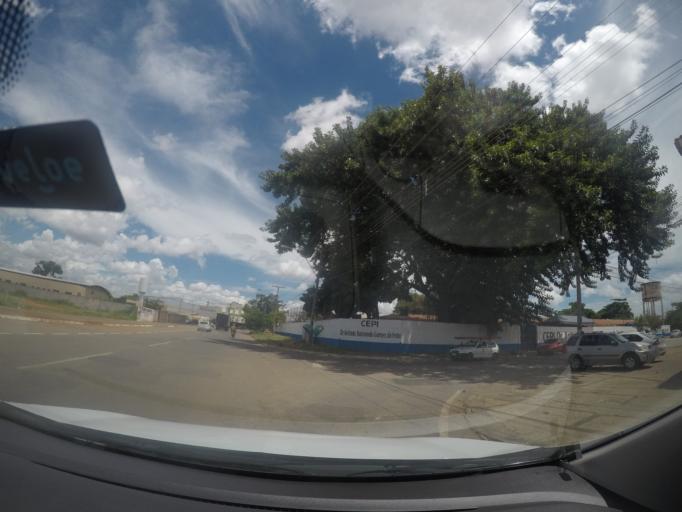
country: BR
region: Goias
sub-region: Goiania
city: Goiania
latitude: -16.6784
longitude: -49.3121
